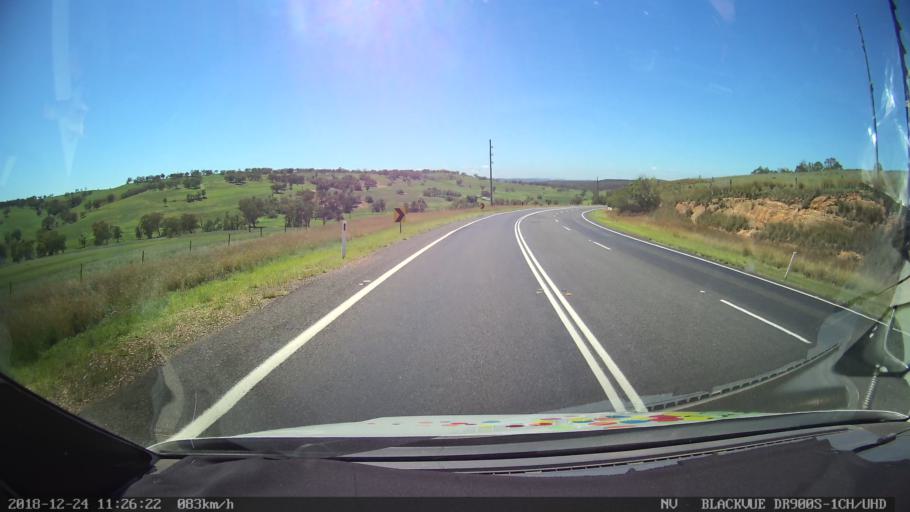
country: AU
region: New South Wales
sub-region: Upper Hunter Shire
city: Merriwa
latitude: -32.1688
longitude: 150.4308
